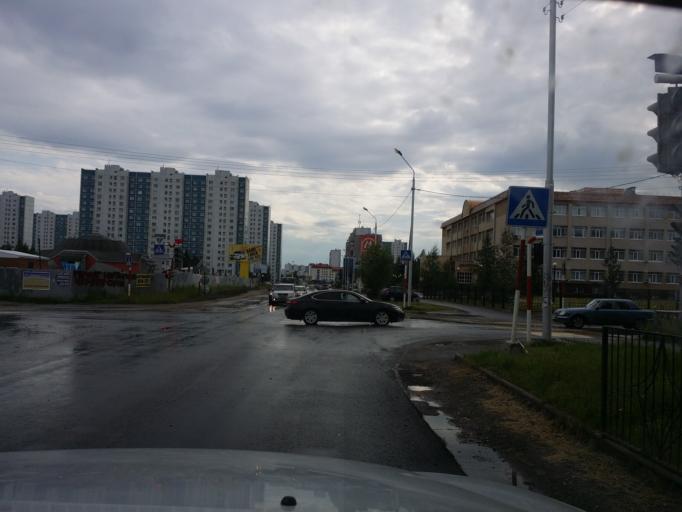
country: RU
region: Khanty-Mansiyskiy Avtonomnyy Okrug
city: Nizhnevartovsk
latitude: 60.9423
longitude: 76.5920
